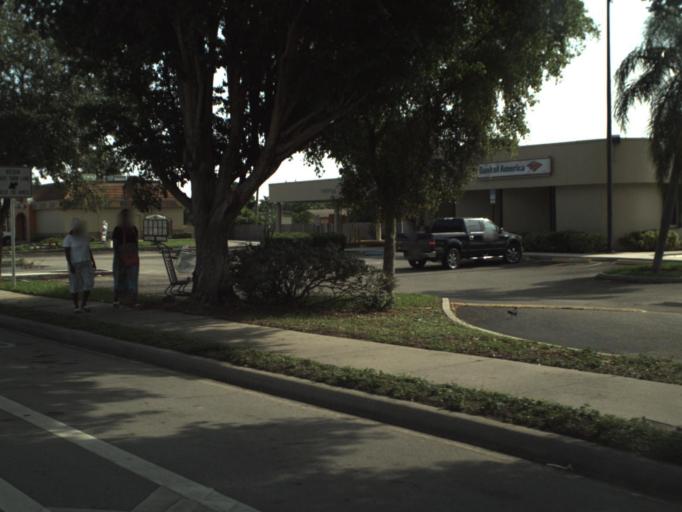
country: US
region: Florida
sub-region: Palm Beach County
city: Belle Glade
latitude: 26.6743
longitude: -80.6704
